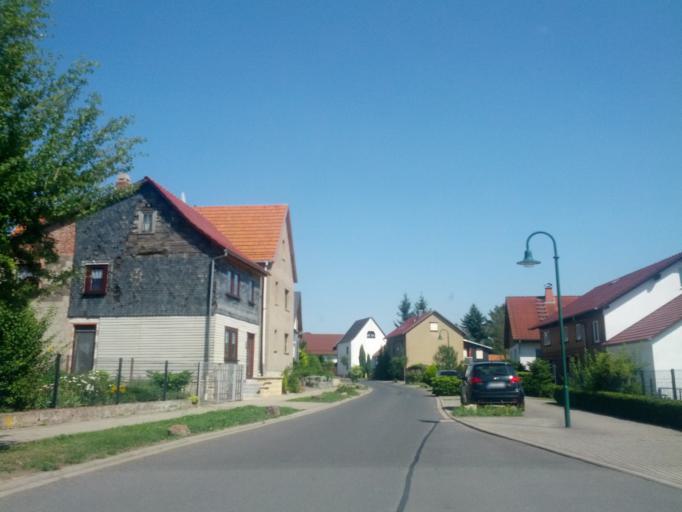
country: DE
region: Thuringia
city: Bischofroda
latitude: 50.9939
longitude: 10.4057
